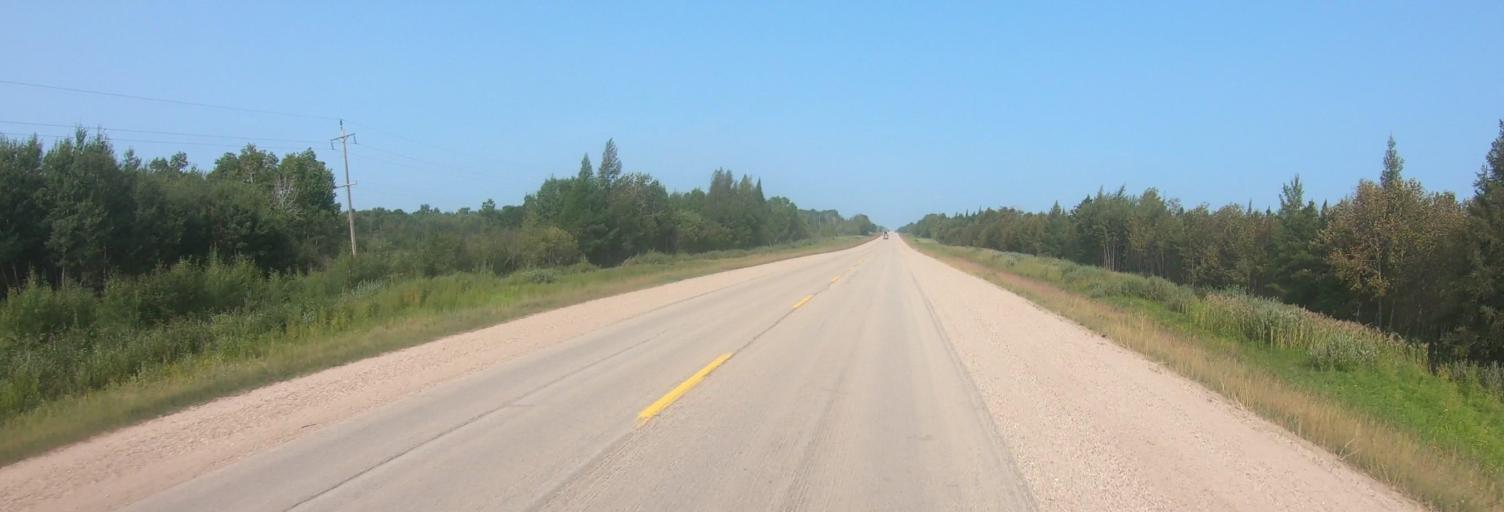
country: US
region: Minnesota
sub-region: Roseau County
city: Roseau
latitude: 49.0418
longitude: -95.7800
